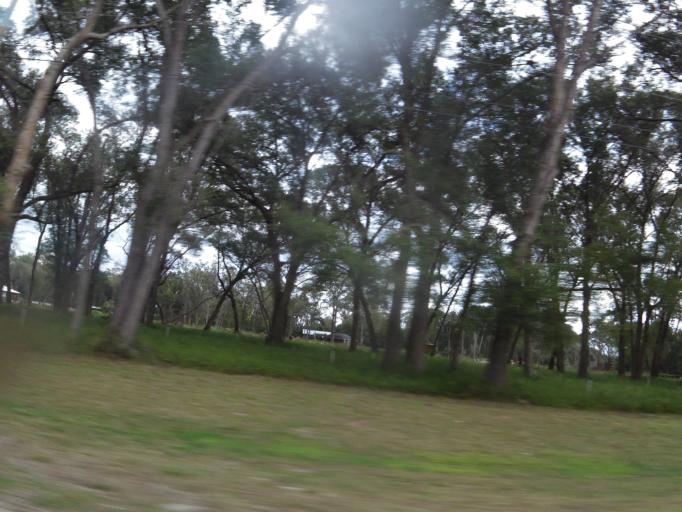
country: US
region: Florida
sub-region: Volusia County
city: Pierson
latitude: 29.3076
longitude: -81.4887
